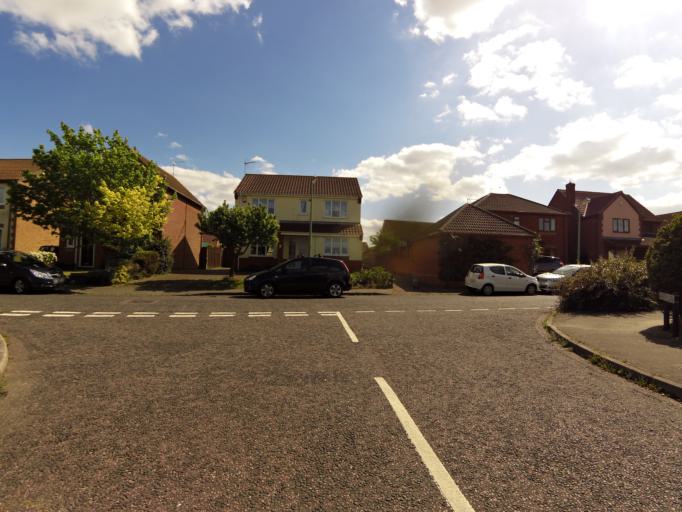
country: GB
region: England
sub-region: Suffolk
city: Kessingland
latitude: 52.4508
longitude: 1.7062
